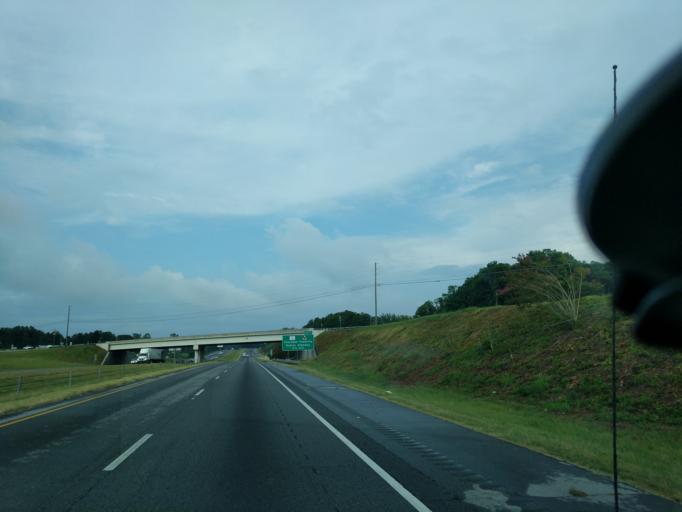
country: US
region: Georgia
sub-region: Franklin County
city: Gumlog
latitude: 34.4732
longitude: -83.0598
